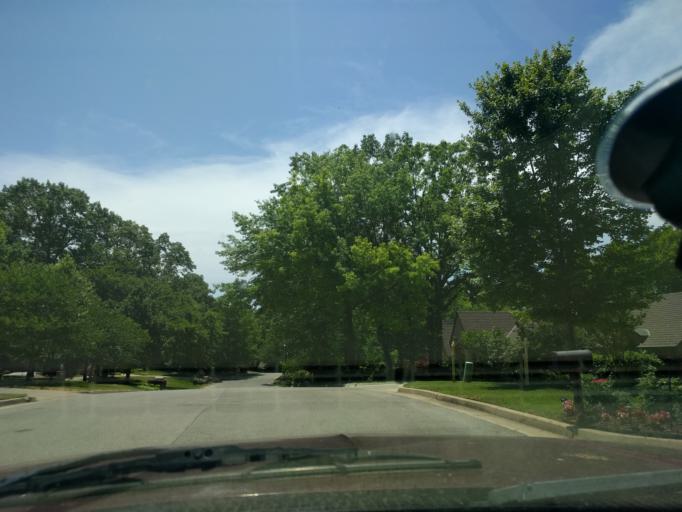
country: US
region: Oklahoma
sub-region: Tulsa County
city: Jenks
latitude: 36.0211
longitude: -95.9386
